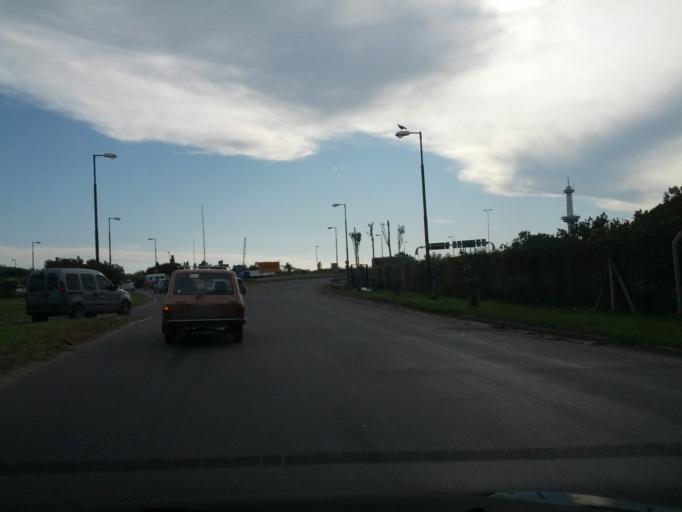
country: AR
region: Buenos Aires F.D.
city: Villa Lugano
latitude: -34.6728
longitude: -58.4349
